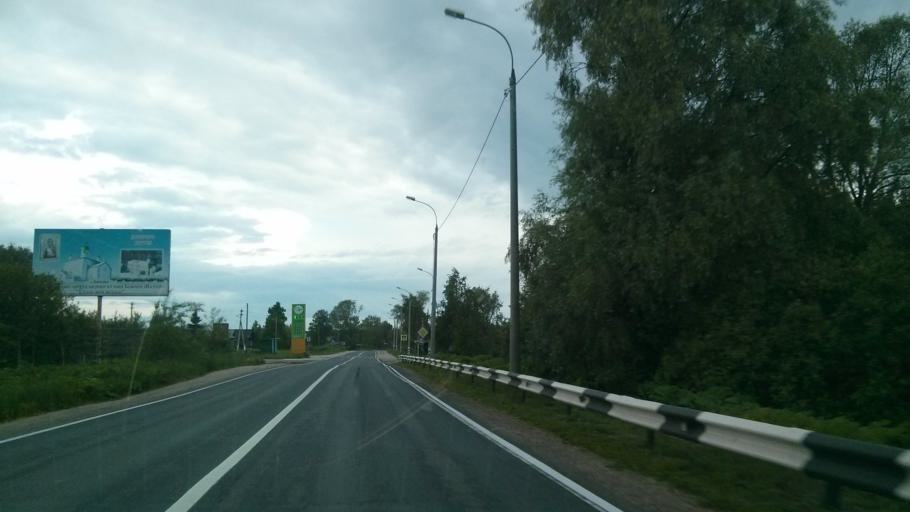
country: RU
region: Nizjnij Novgorod
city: Vacha
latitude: 55.7556
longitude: 42.5190
